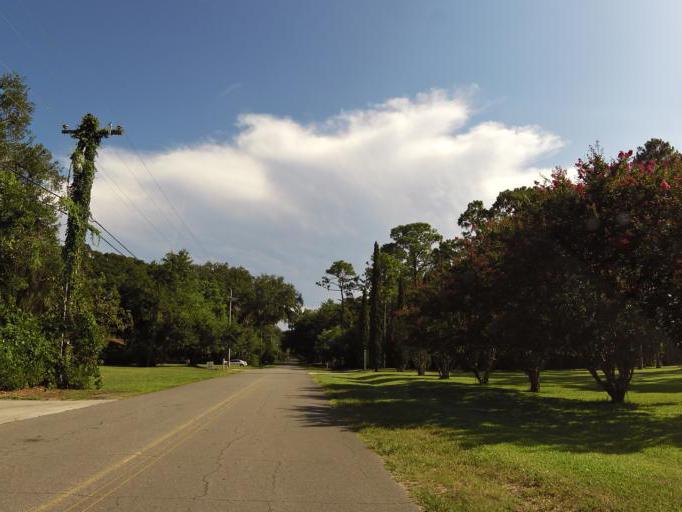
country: US
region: Florida
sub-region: Nassau County
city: Fernandina Beach
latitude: 30.6495
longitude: -81.4628
